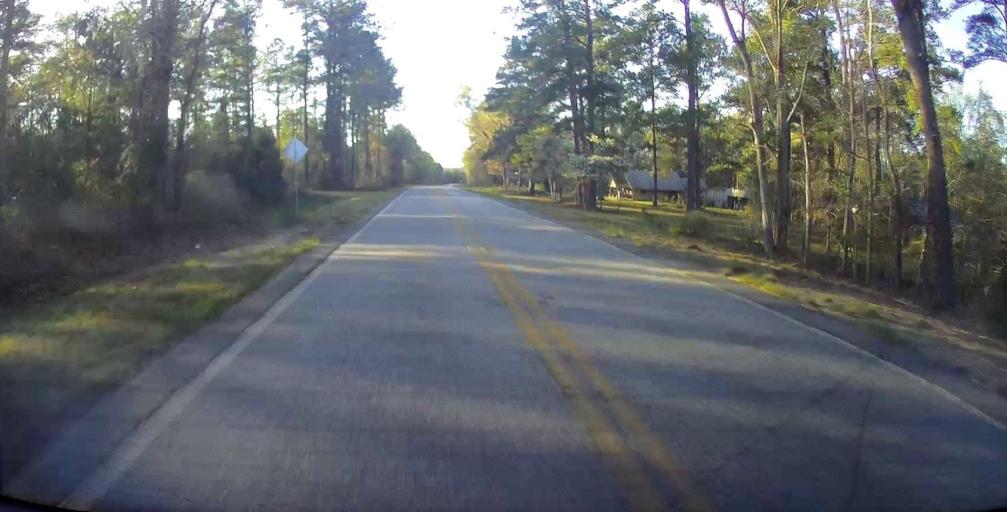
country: US
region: Georgia
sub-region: Wilcox County
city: Abbeville
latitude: 32.0670
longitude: -83.2779
